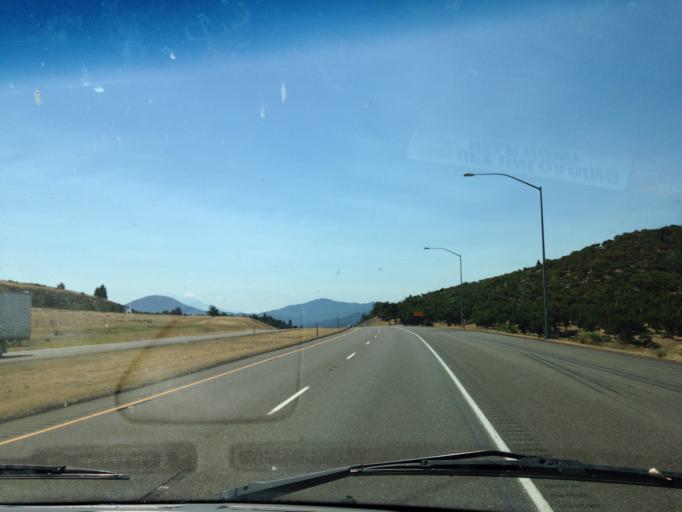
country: US
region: Oregon
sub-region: Jackson County
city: Ashland
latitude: 41.9847
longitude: -122.6076
